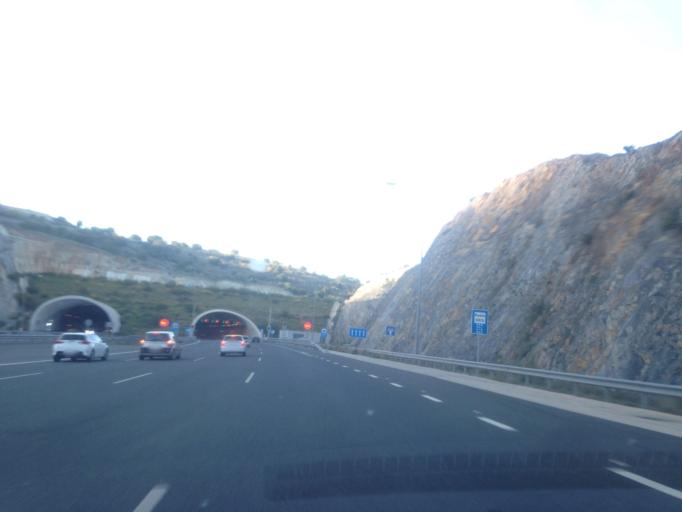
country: ES
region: Andalusia
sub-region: Provincia de Malaga
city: Torremolinos
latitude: 36.6473
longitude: -4.5125
